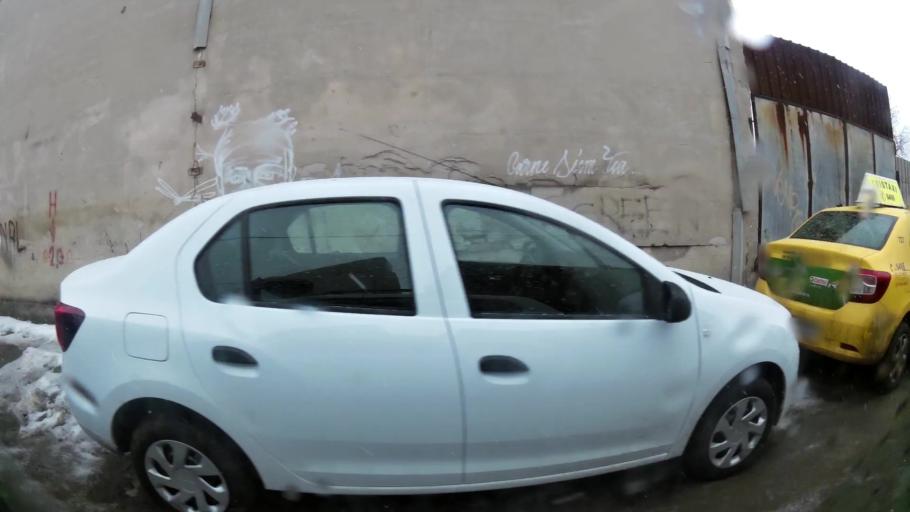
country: RO
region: Ilfov
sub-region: Comuna Chiajna
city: Rosu
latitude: 44.4296
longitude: 26.0075
